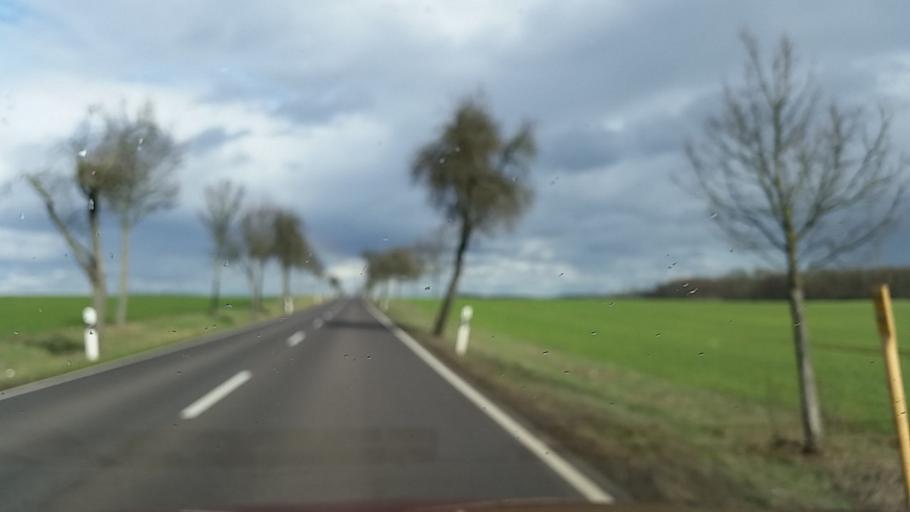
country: DE
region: Saxony-Anhalt
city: Rohrberg
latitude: 52.7412
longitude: 11.0652
